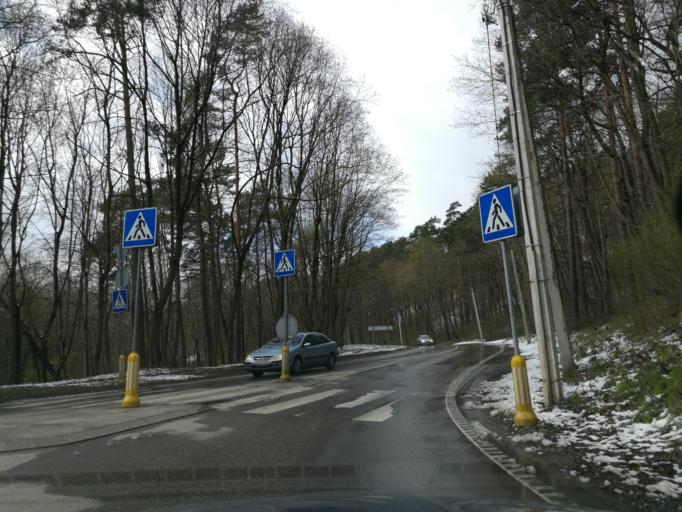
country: LT
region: Kauno apskritis
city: Dainava (Kaunas)
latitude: 54.8704
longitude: 23.9816
